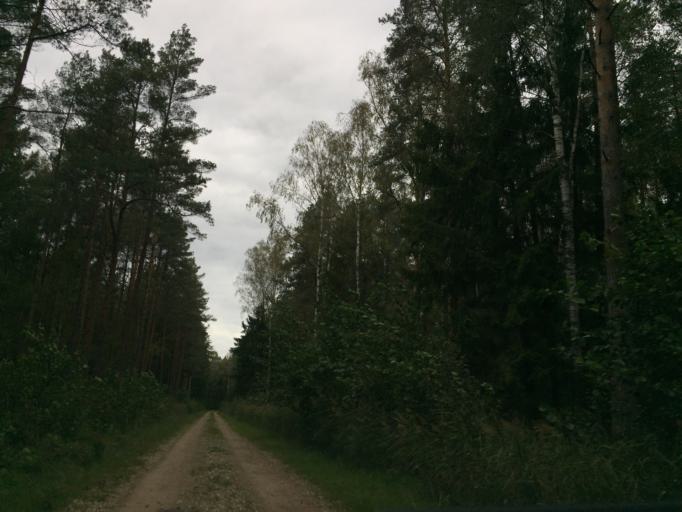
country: LV
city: Tireli
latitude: 56.8898
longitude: 23.5441
